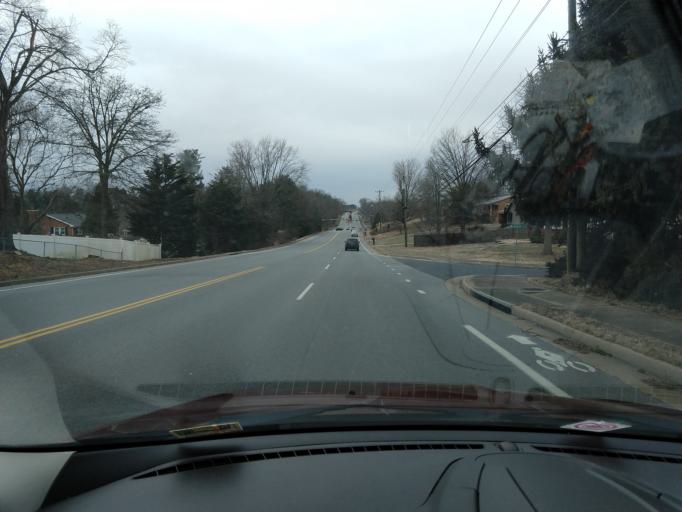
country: US
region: Virginia
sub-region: City of Waynesboro
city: Waynesboro
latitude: 38.0686
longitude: -78.9185
